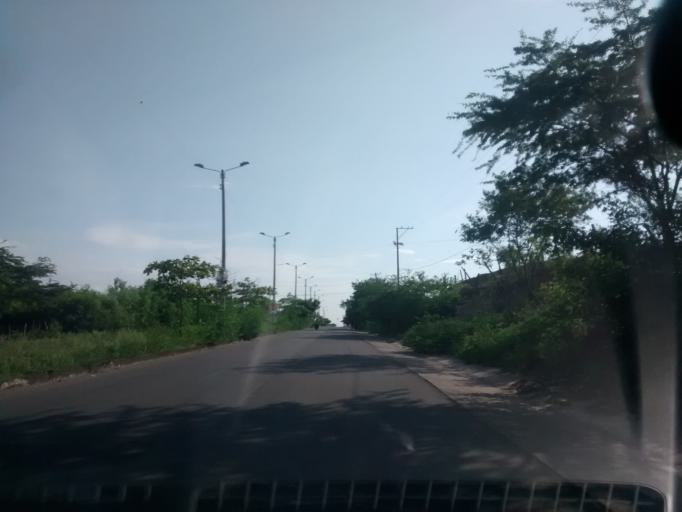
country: CO
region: Cundinamarca
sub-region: Girardot
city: Girardot City
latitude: 4.3170
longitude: -74.8075
